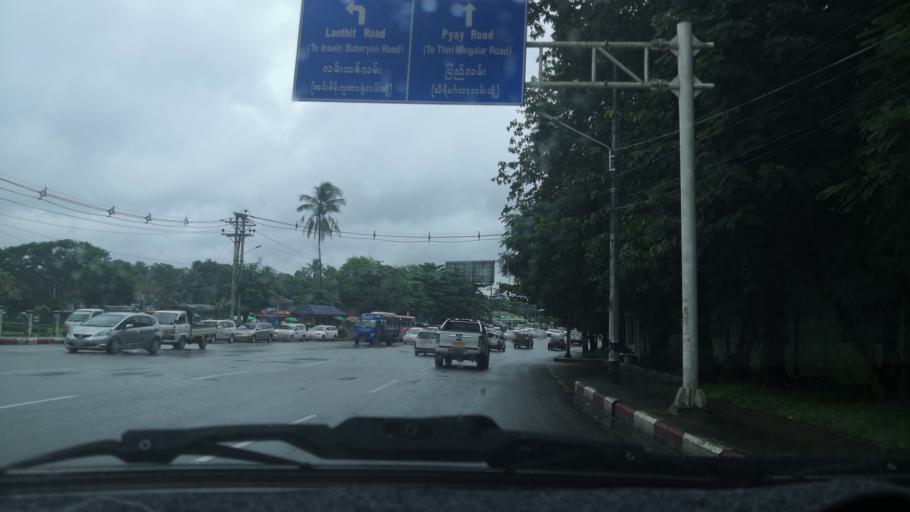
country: MM
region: Yangon
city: Yangon
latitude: 16.8914
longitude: 96.1201
